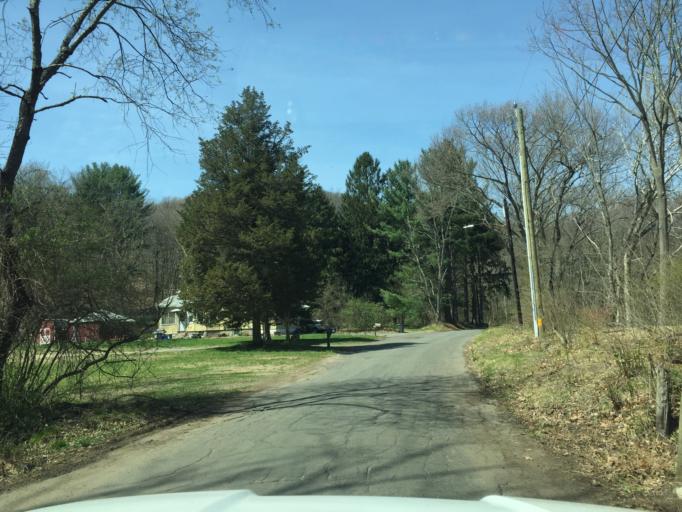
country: US
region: Connecticut
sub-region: New Haven County
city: Naugatuck
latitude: 41.4447
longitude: -73.0693
